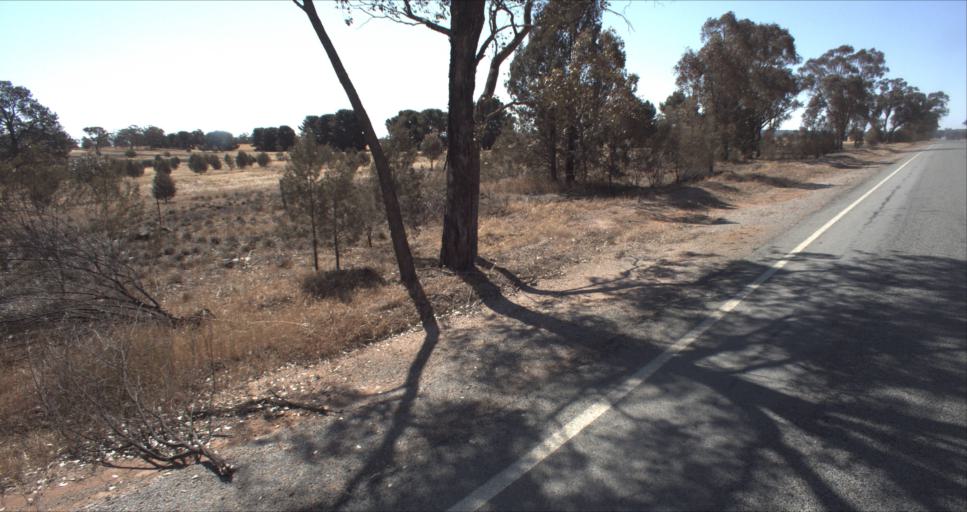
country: AU
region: New South Wales
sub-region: Leeton
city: Leeton
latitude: -34.4800
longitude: 146.4344
